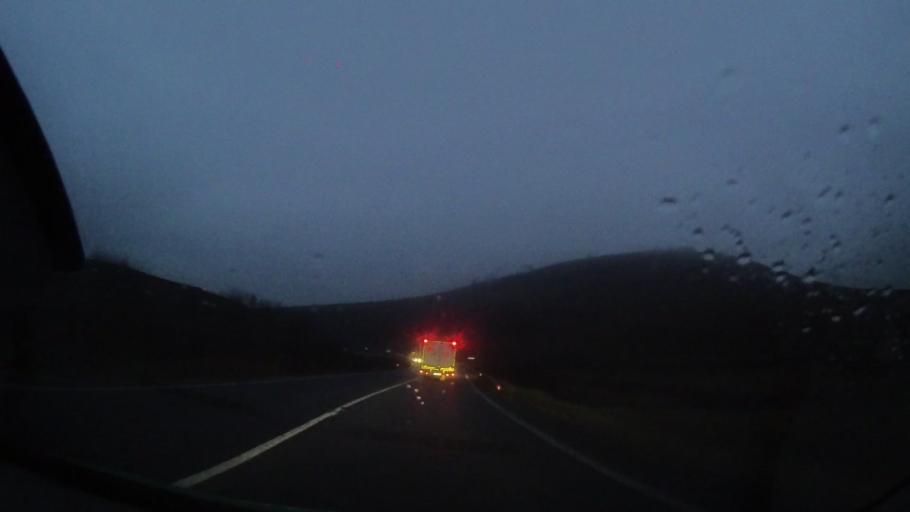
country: RO
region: Harghita
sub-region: Comuna Subcetate
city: Subcetate
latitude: 46.8385
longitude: 25.4842
